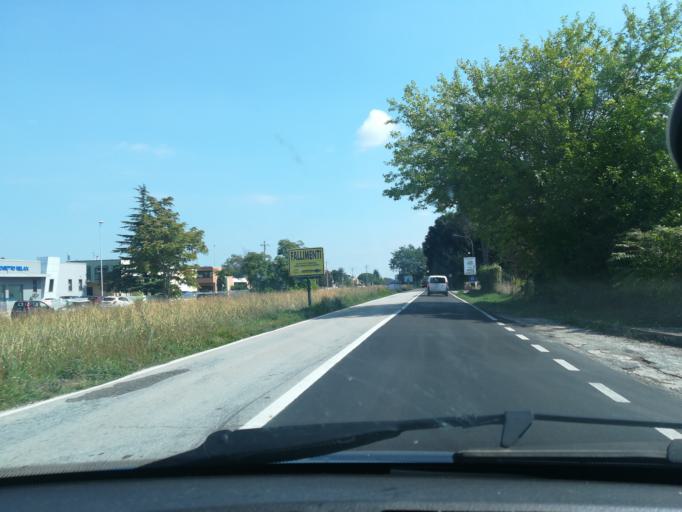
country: IT
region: The Marches
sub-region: Provincia di Macerata
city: Tolentino
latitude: 43.2202
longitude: 13.3182
